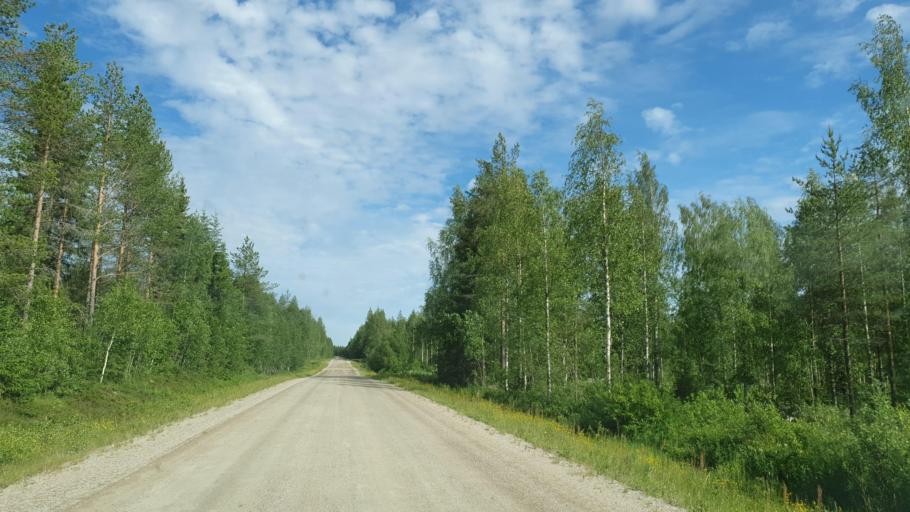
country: FI
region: Kainuu
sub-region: Kehys-Kainuu
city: Kuhmo
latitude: 64.5147
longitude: 29.4115
